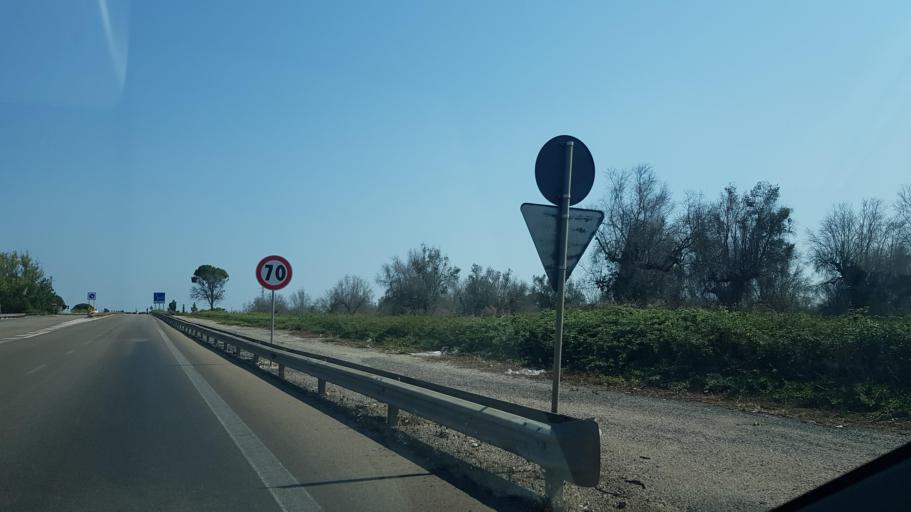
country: IT
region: Apulia
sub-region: Provincia di Lecce
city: Muro Leccese
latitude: 40.1073
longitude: 18.3183
